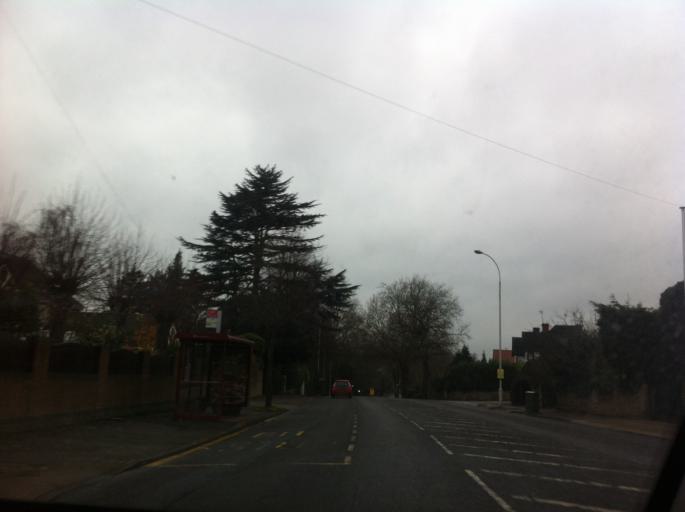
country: GB
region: England
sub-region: Northamptonshire
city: Earls Barton
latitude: 52.2647
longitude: -0.7466
